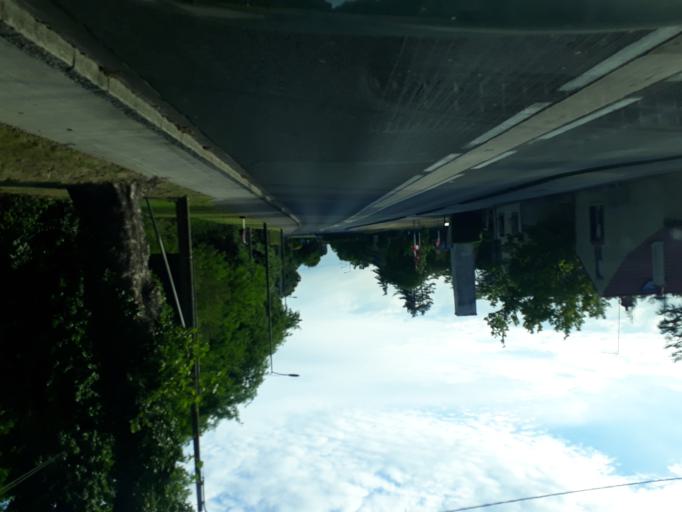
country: FR
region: Centre
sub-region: Departement du Loiret
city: La Ferte-Saint-Aubin
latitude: 47.7287
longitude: 1.9387
